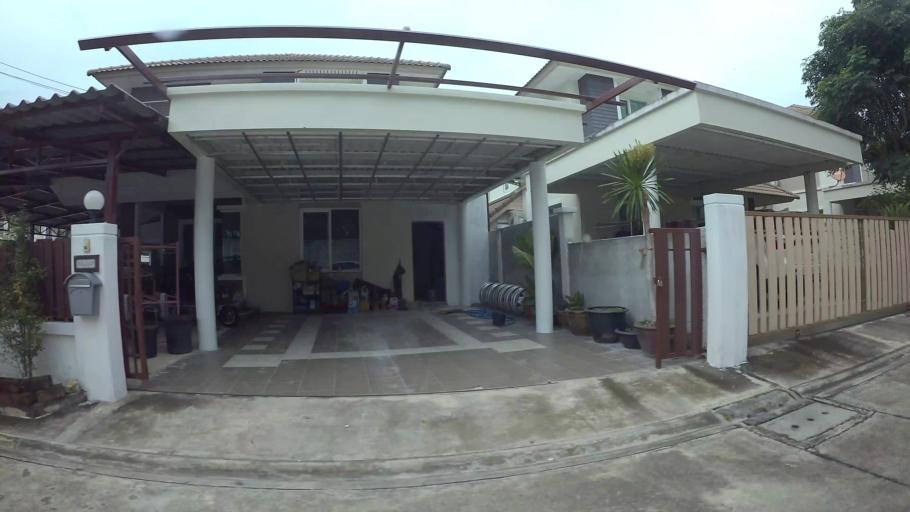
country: TH
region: Chon Buri
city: Si Racha
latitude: 13.1432
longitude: 100.9813
